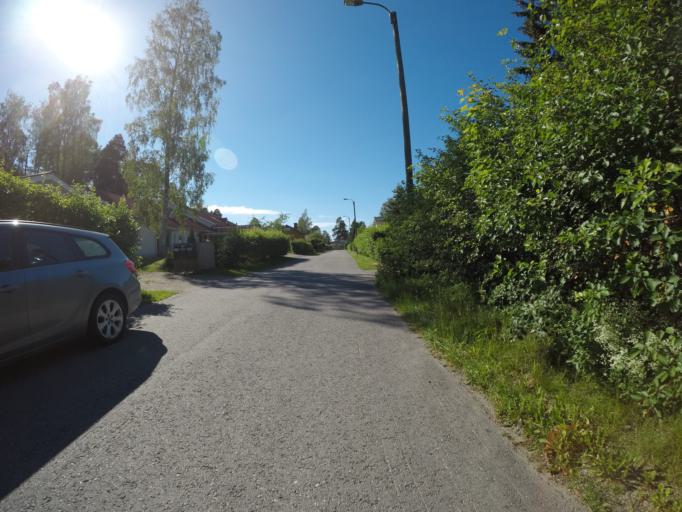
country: FI
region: Haeme
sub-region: Haemeenlinna
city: Haemeenlinna
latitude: 61.0092
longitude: 24.4808
